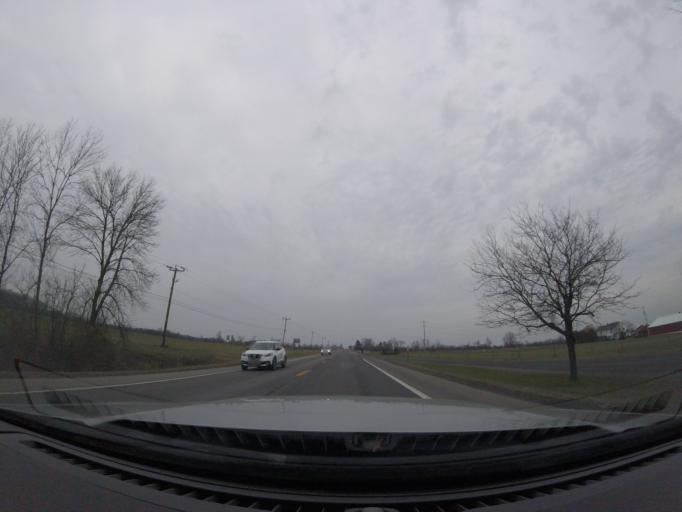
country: US
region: New York
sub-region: Yates County
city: Dundee
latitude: 42.6193
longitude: -76.9438
